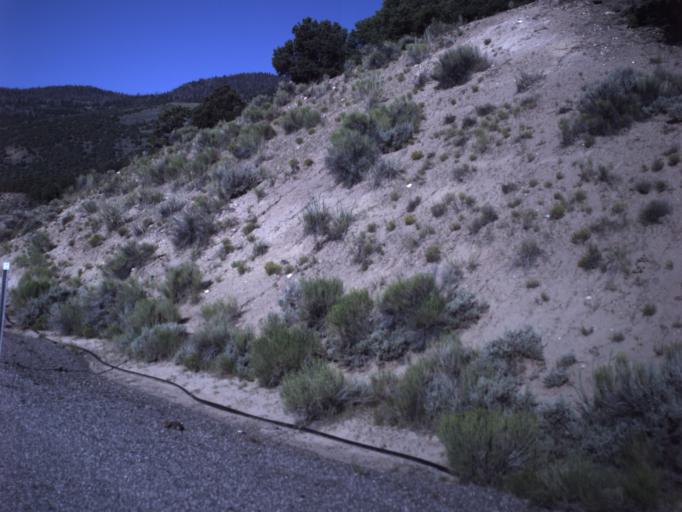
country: US
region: Utah
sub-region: Wayne County
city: Loa
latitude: 38.6240
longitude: -111.4517
